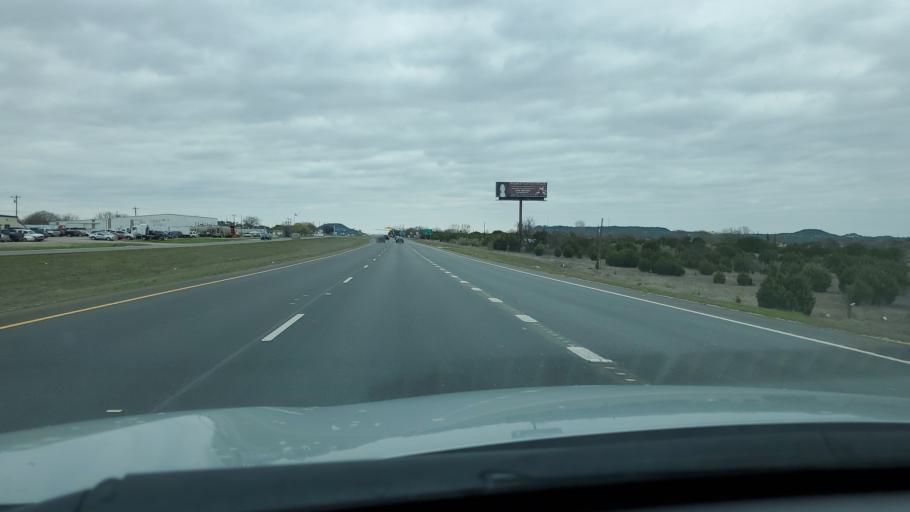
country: US
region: Texas
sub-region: Bell County
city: Killeen
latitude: 31.0174
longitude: -97.7532
